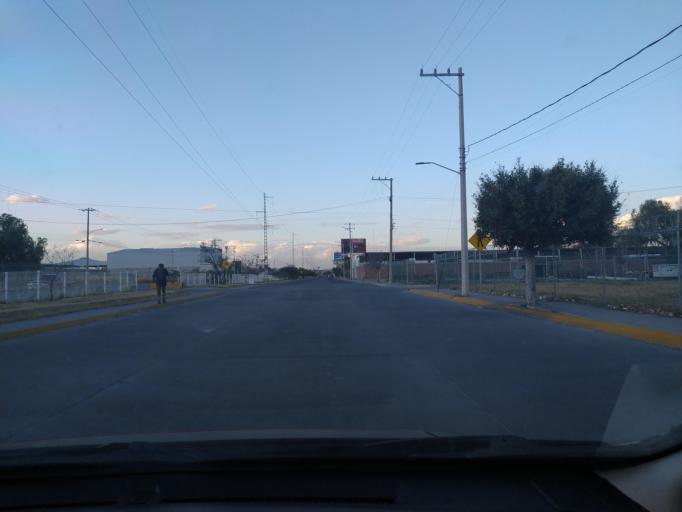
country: LA
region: Oudomxai
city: Muang La
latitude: 21.0196
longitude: 101.8695
